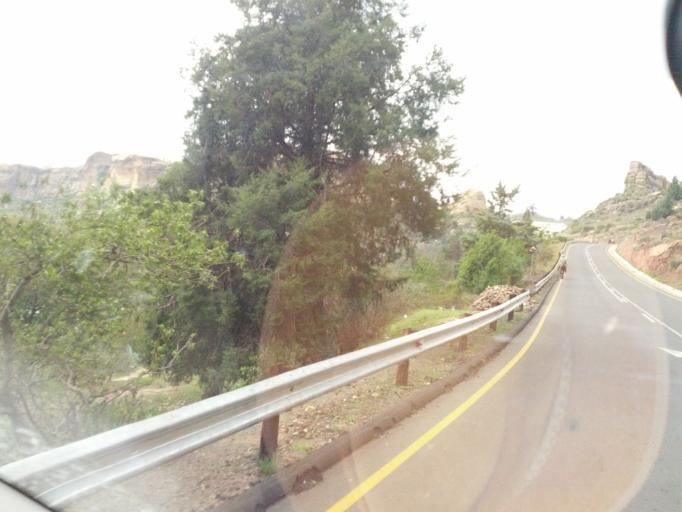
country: LS
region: Maseru
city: Nako
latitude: -29.4770
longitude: 27.7384
